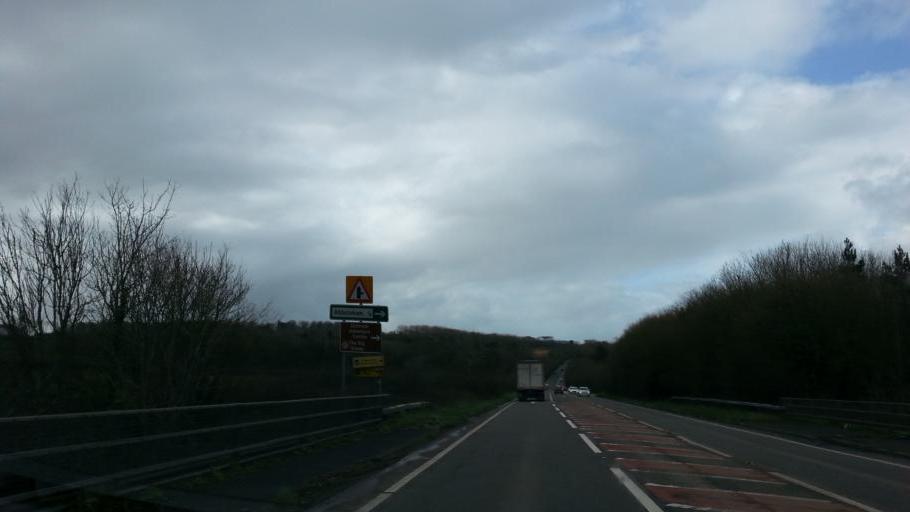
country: GB
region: England
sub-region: Devon
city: Northam
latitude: 51.0176
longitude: -4.2395
